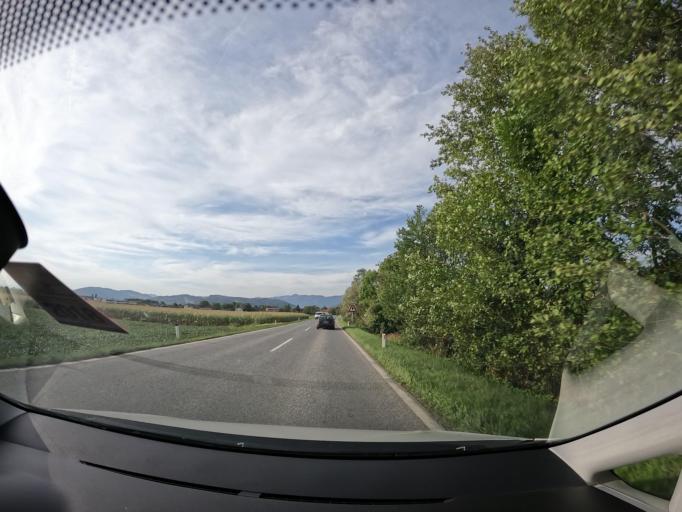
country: AT
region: Carinthia
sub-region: Politischer Bezirk Volkermarkt
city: Eberndorf
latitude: 46.6148
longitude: 14.6357
